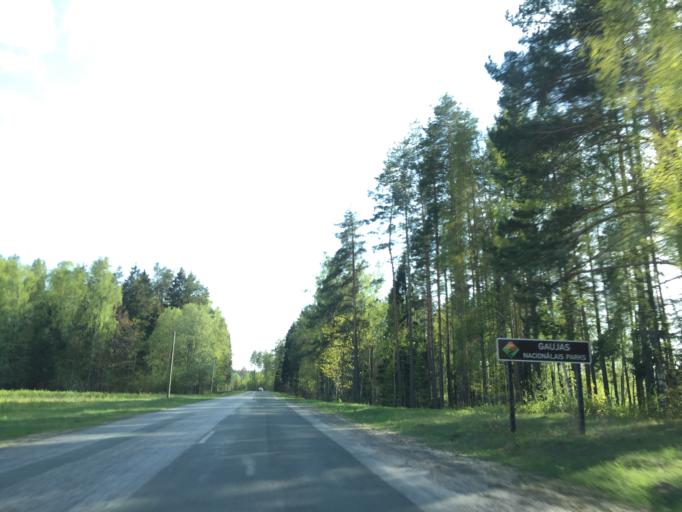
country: LV
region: Sigulda
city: Sigulda
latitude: 57.2479
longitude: 24.8692
